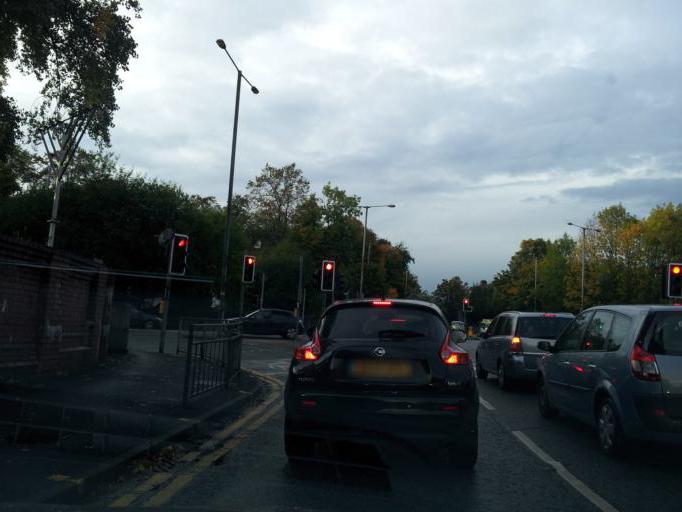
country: GB
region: England
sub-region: Manchester
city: Crumpsall
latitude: 53.5155
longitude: -2.2489
